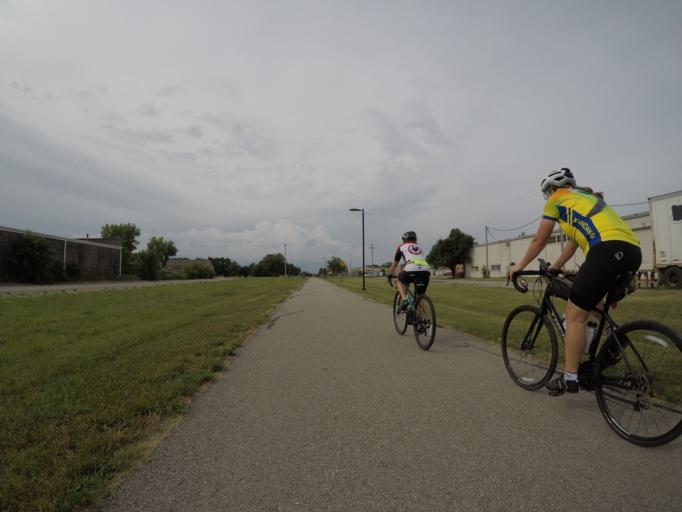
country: US
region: Kansas
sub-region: Franklin County
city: Ottawa
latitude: 38.5910
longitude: -95.2705
